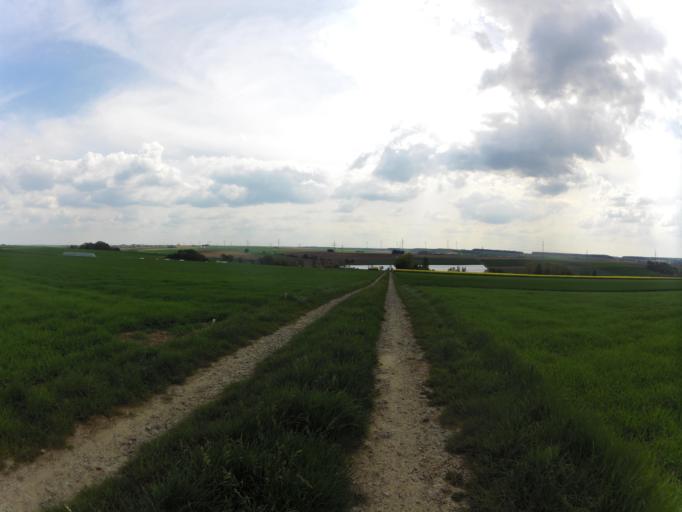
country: DE
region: Bavaria
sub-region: Regierungsbezirk Unterfranken
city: Sulzdorf
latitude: 49.6283
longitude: 9.9126
